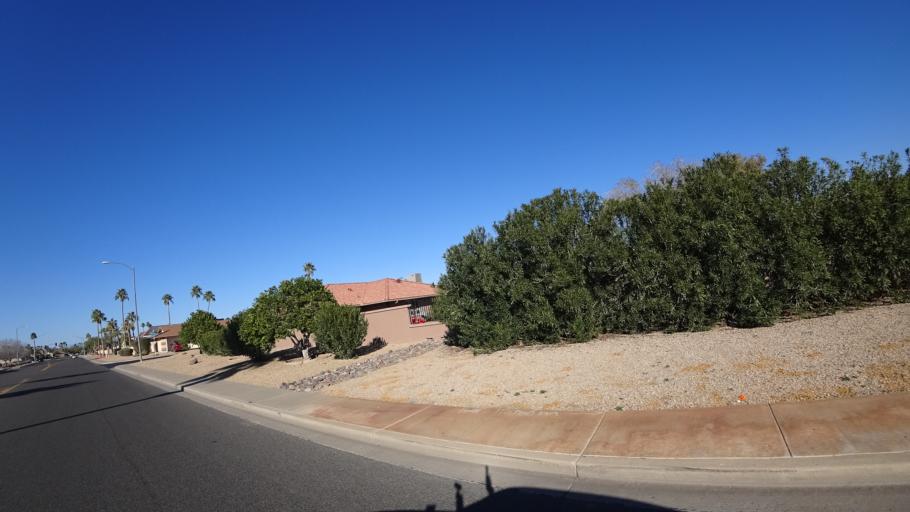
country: US
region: Arizona
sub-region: Maricopa County
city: Sun City West
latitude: 33.6767
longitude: -112.3544
